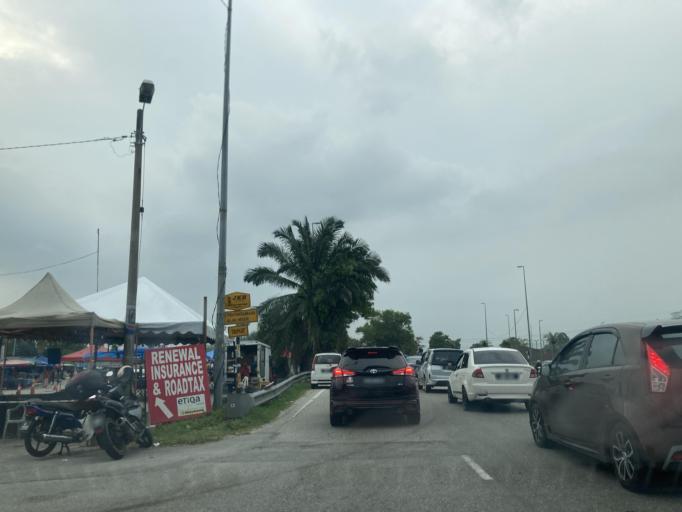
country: MY
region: Selangor
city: Kampung Baru Subang
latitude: 3.2007
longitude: 101.5481
